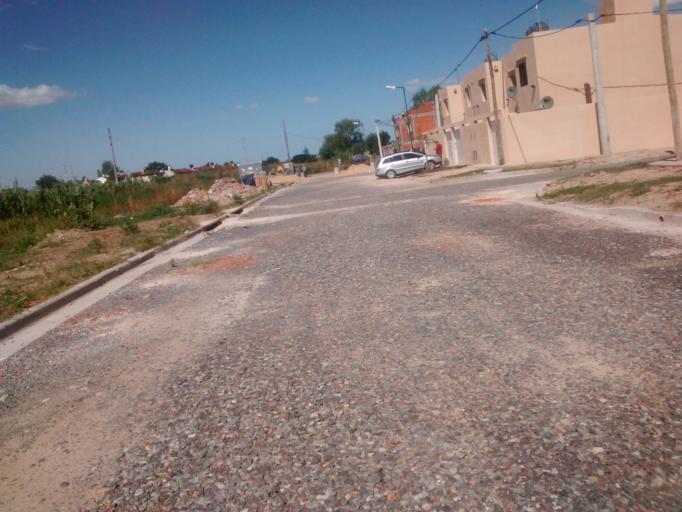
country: AR
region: Buenos Aires
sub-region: Partido de La Plata
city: La Plata
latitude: -34.9345
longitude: -57.9090
